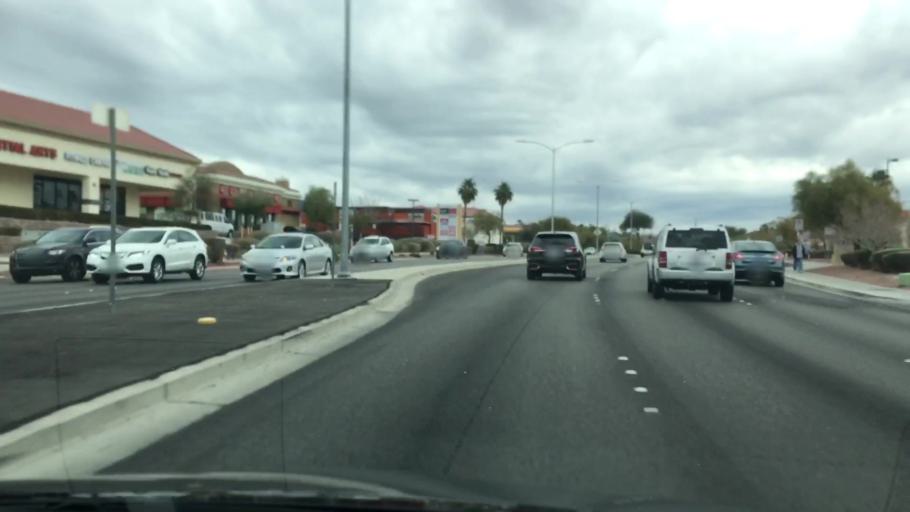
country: US
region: Nevada
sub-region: Clark County
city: Whitney
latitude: 35.9954
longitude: -115.1011
